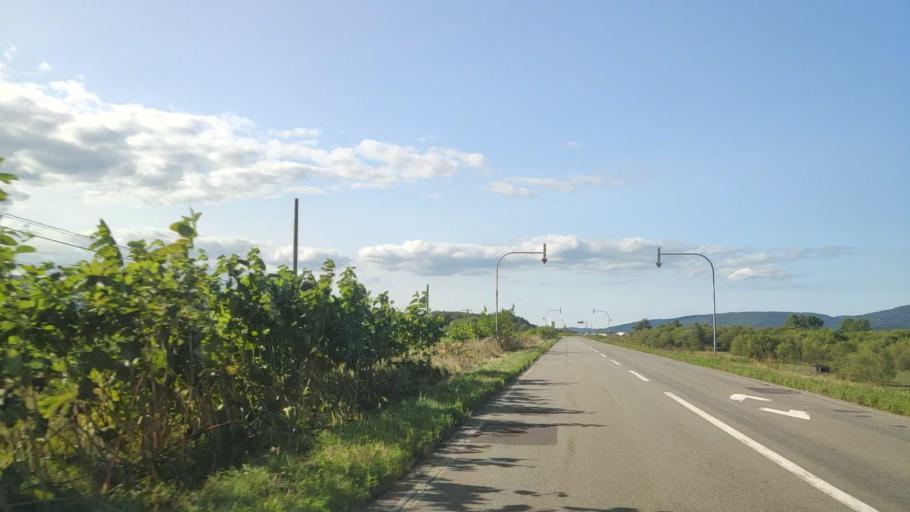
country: JP
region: Hokkaido
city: Nayoro
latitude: 44.8078
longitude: 142.0667
